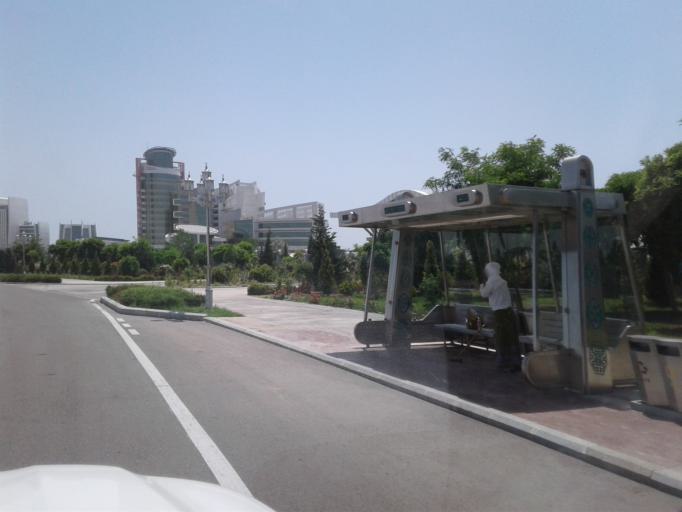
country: TM
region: Balkan
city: Turkmenbasy
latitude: 39.9642
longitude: 52.8334
